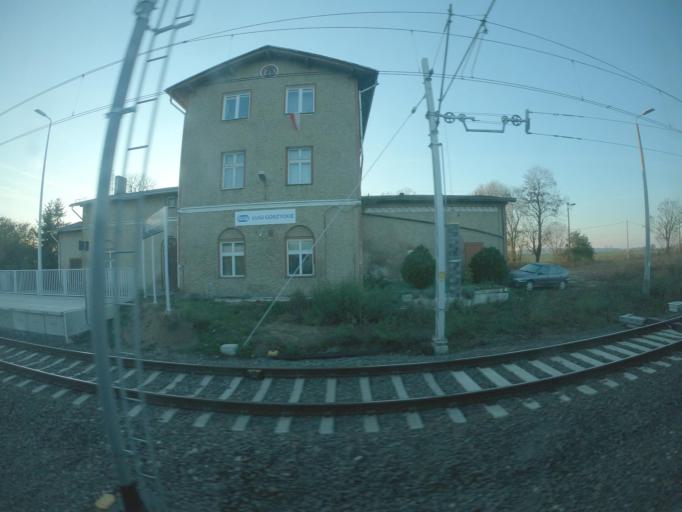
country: PL
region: Lubusz
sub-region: Powiat slubicki
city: Gorzyca
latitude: 52.5161
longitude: 14.6510
